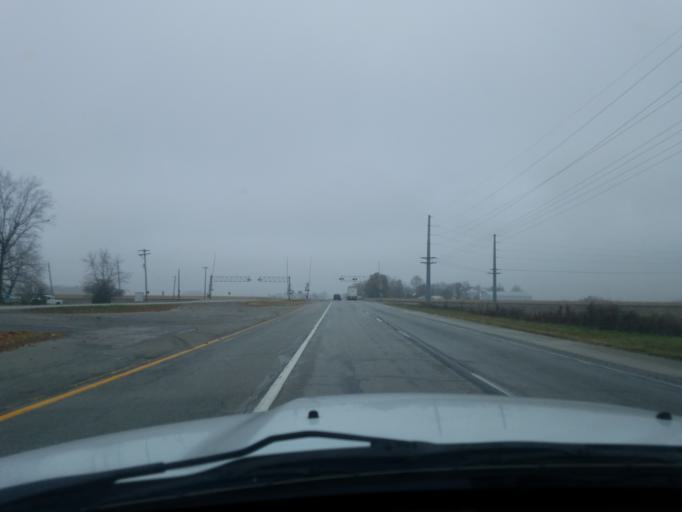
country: US
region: Indiana
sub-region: Tipton County
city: Tipton
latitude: 40.2881
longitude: -86.1269
